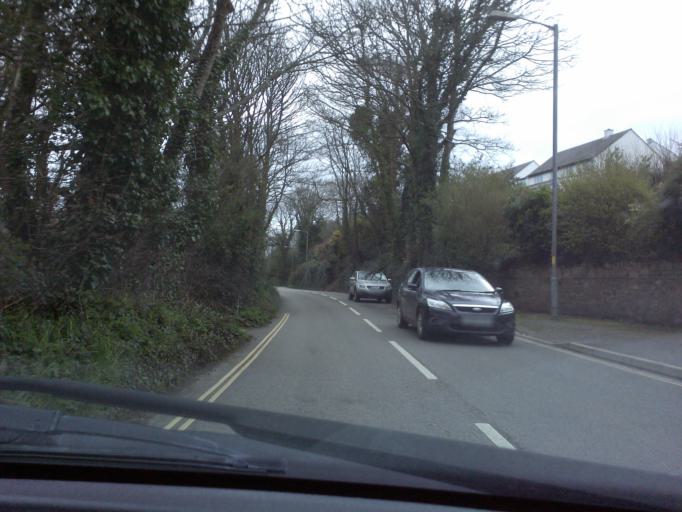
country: GB
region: England
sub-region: Cornwall
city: Penzance
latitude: 50.1092
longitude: -5.5572
